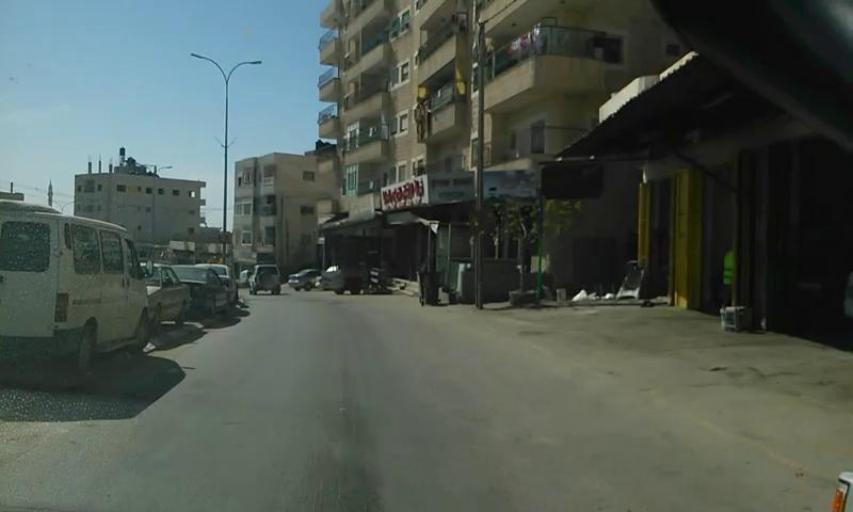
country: PS
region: West Bank
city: Al `Ayzariyah
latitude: 31.7607
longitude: 35.2813
